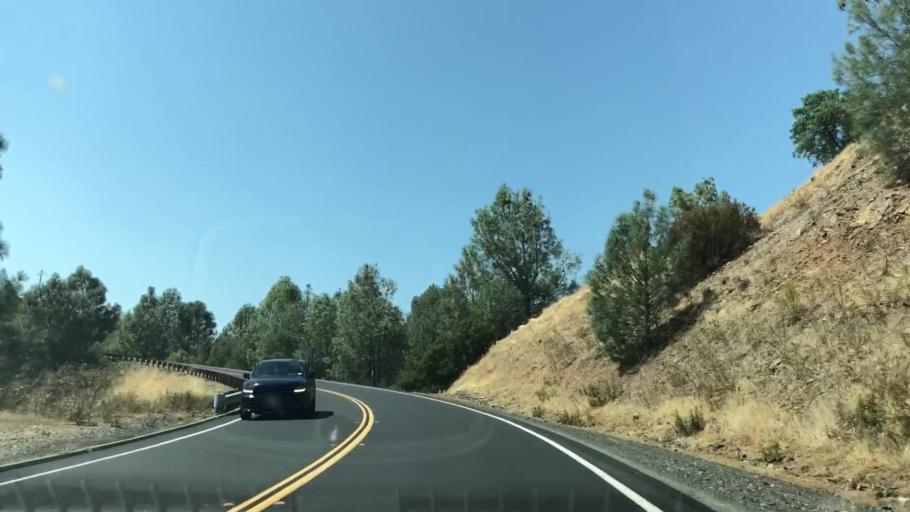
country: US
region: California
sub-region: Tuolumne County
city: Tuolumne City
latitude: 37.8189
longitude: -120.3048
